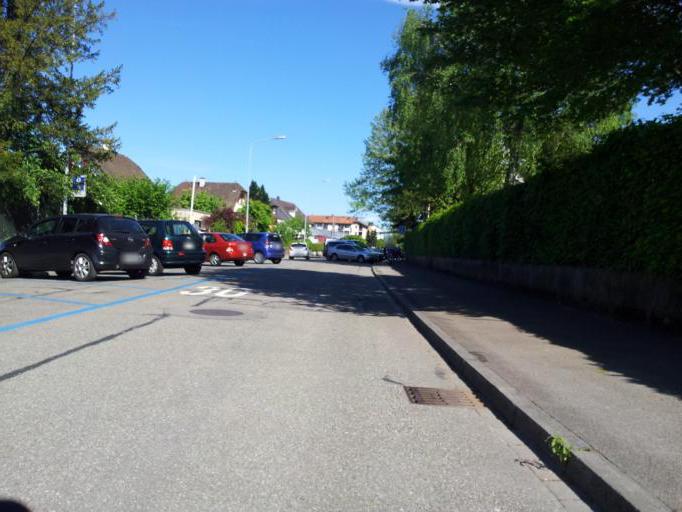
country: CH
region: Zurich
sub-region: Bezirk Dietikon
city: Schlieren / Boden
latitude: 47.3972
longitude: 8.4577
